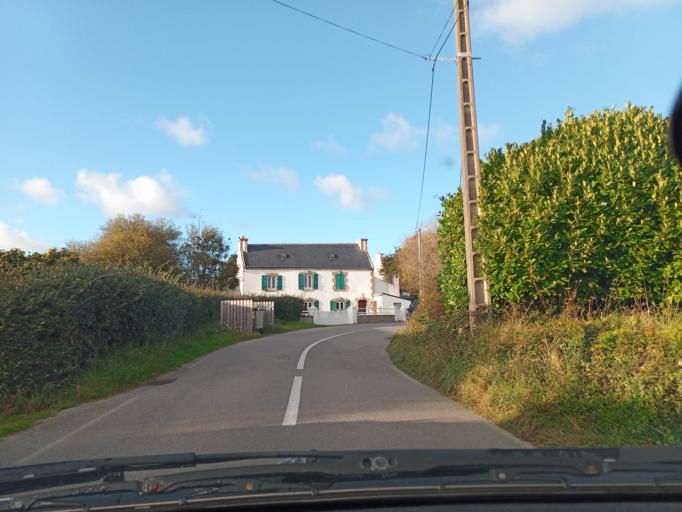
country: FR
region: Brittany
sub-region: Departement du Finistere
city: Esquibien
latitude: 48.0162
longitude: -4.5652
